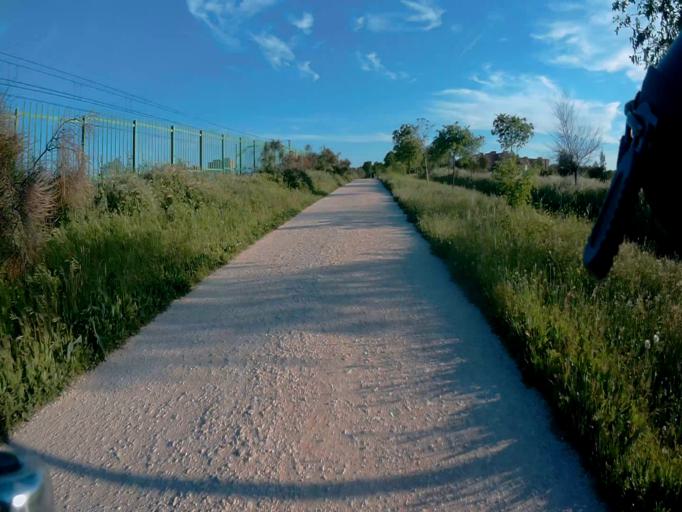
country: ES
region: Madrid
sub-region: Provincia de Madrid
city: Fuenlabrada
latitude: 40.2998
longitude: -3.7910
